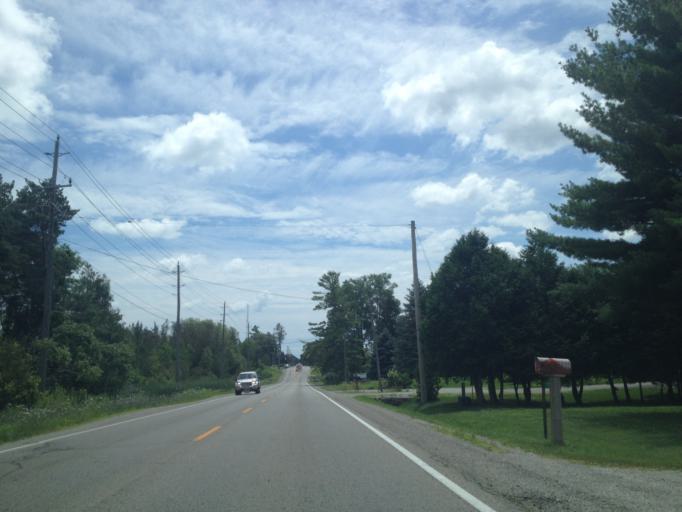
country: CA
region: Ontario
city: Norfolk County
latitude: 42.8323
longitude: -80.3381
